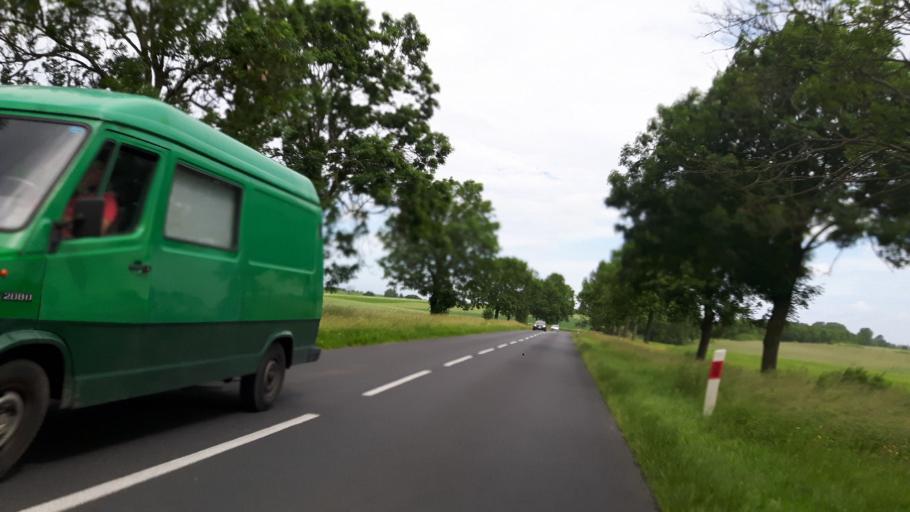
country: PL
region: West Pomeranian Voivodeship
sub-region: Powiat gryficki
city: Trzebiatow
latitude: 54.0275
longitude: 15.2410
